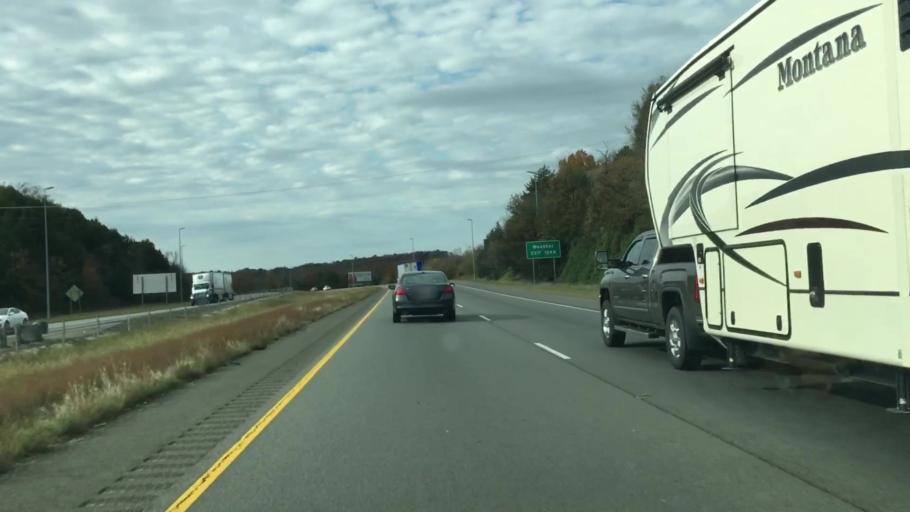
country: US
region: Arkansas
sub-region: Faulkner County
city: Conway
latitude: 35.1165
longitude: -92.4488
